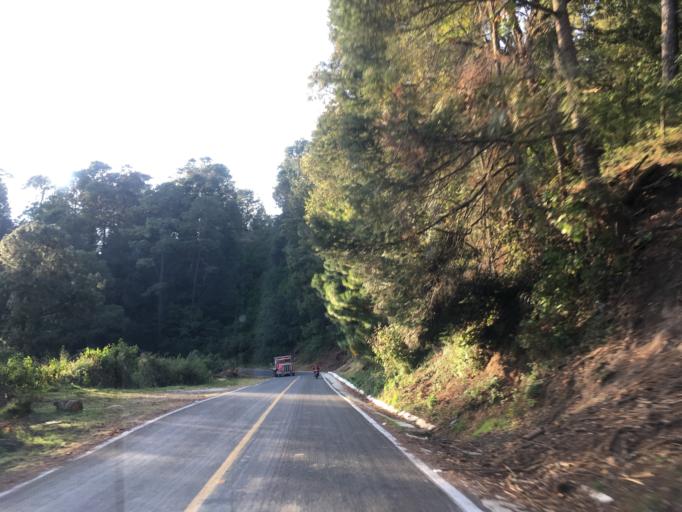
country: MX
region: Michoacan
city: Tzitzio
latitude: 19.6814
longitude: -100.8923
